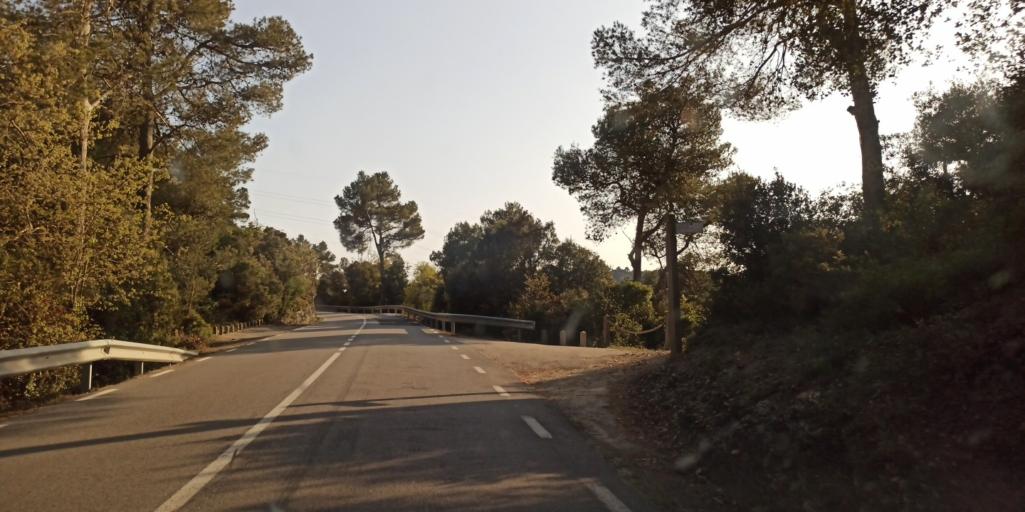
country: ES
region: Catalonia
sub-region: Provincia de Barcelona
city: Sant Just Desvern
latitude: 41.4235
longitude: 2.0615
